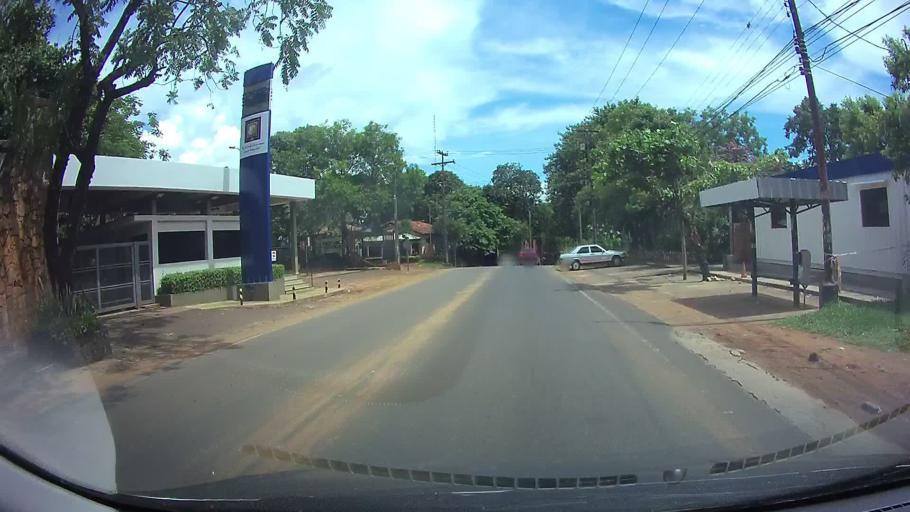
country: PY
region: Central
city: San Lorenzo
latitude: -25.3024
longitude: -57.4910
